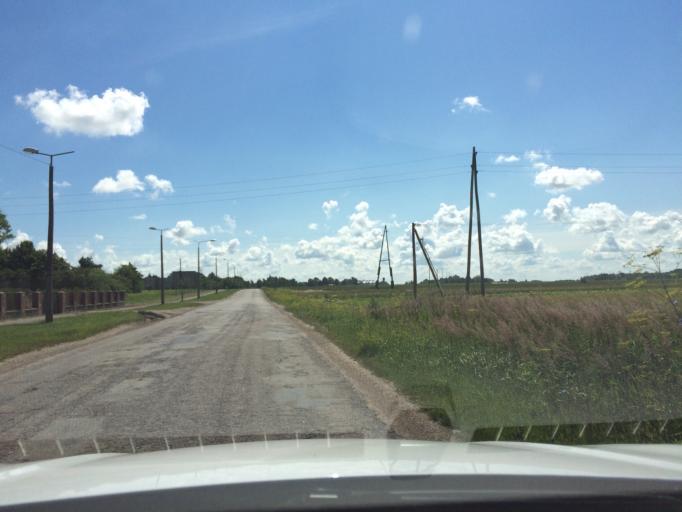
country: LV
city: Tervete
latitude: 56.5254
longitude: 23.5102
